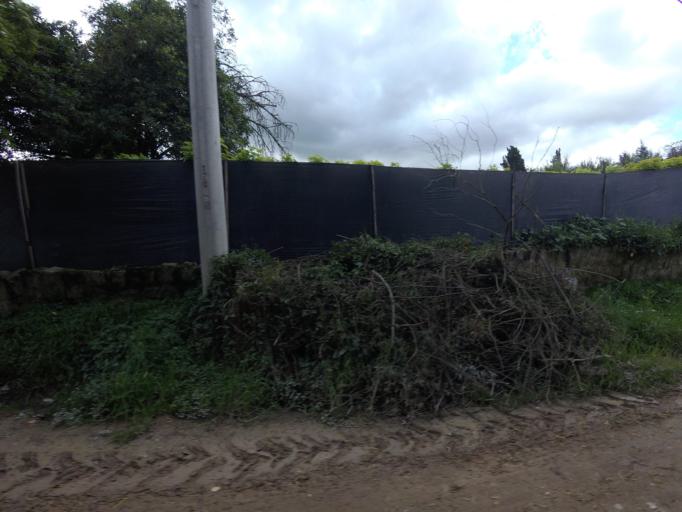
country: CO
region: Cundinamarca
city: Tabio
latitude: 4.9317
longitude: -74.0915
